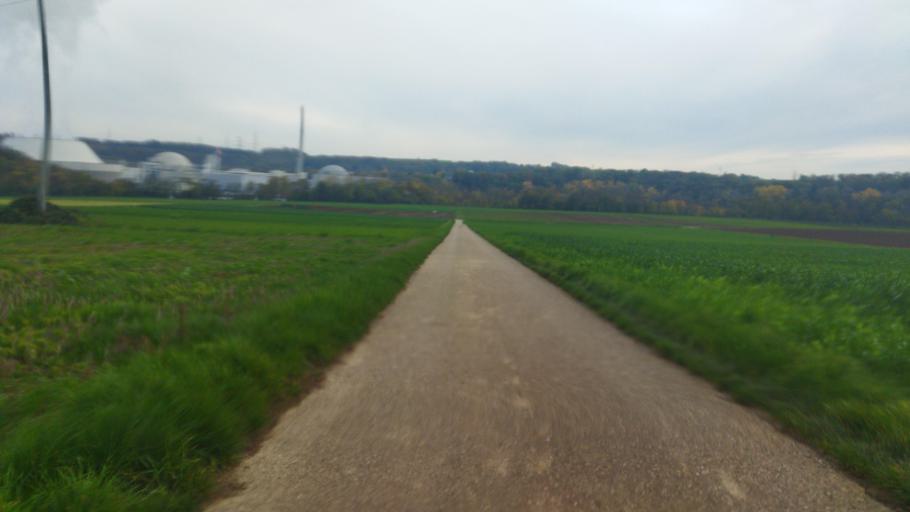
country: DE
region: Baden-Wuerttemberg
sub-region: Regierungsbezirk Stuttgart
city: Neckarwestheim
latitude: 49.0498
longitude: 9.1665
